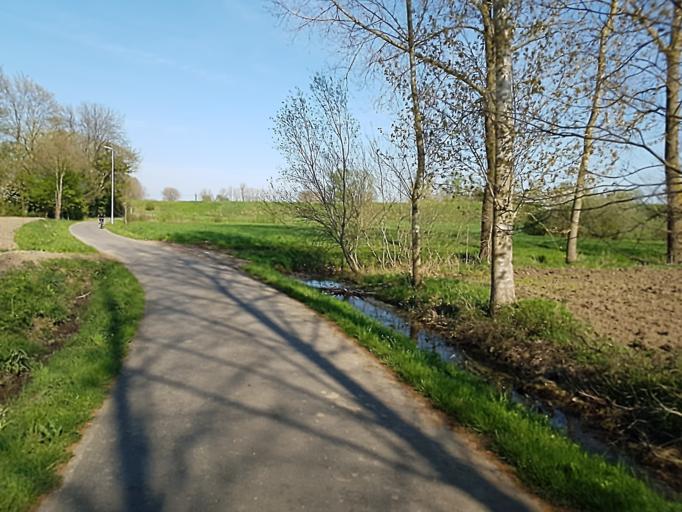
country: BE
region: Flanders
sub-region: Provincie Oost-Vlaanderen
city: Temse
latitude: 51.1541
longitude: 4.2101
